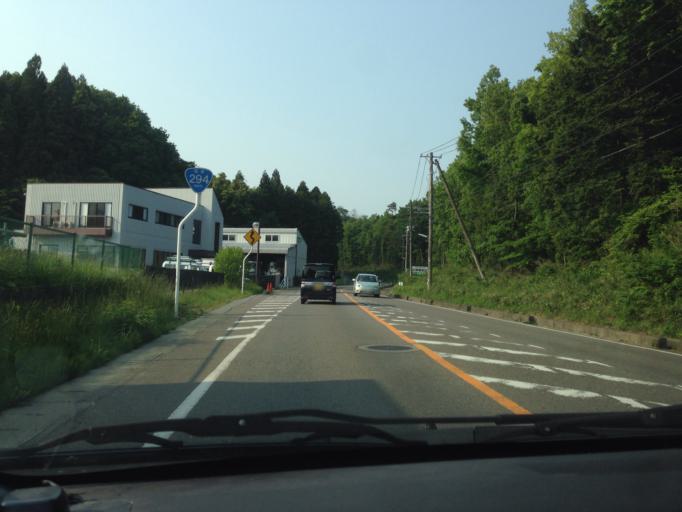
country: JP
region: Tochigi
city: Kuroiso
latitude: 37.1060
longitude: 140.1975
